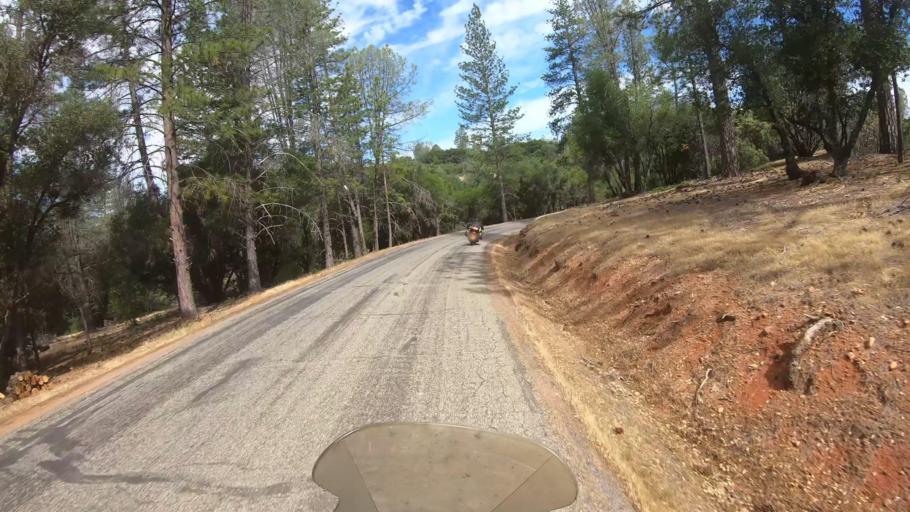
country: US
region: California
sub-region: Tuolumne County
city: Tuolumne City
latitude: 37.8287
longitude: -120.1193
